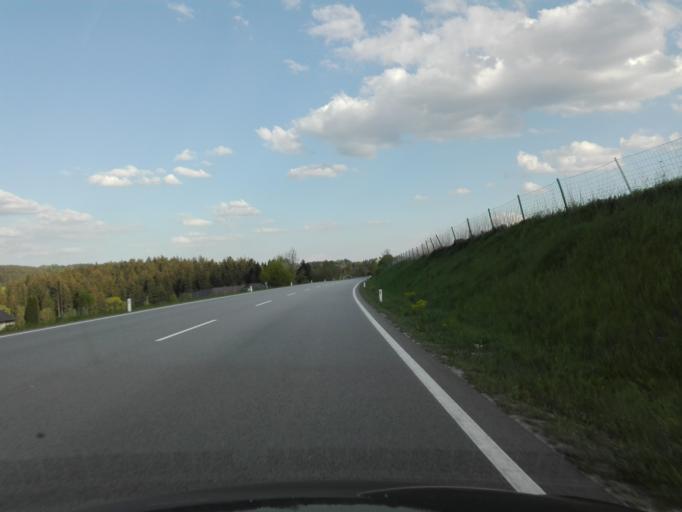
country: AT
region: Upper Austria
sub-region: Politischer Bezirk Rohrbach
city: Kleinzell im Muehlkreis
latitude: 48.4677
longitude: 14.0154
